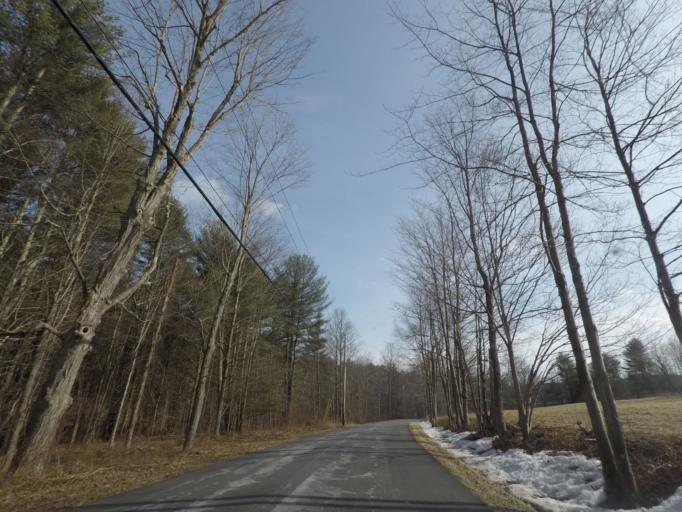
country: US
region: New York
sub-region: Rensselaer County
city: Nassau
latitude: 42.5064
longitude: -73.5541
